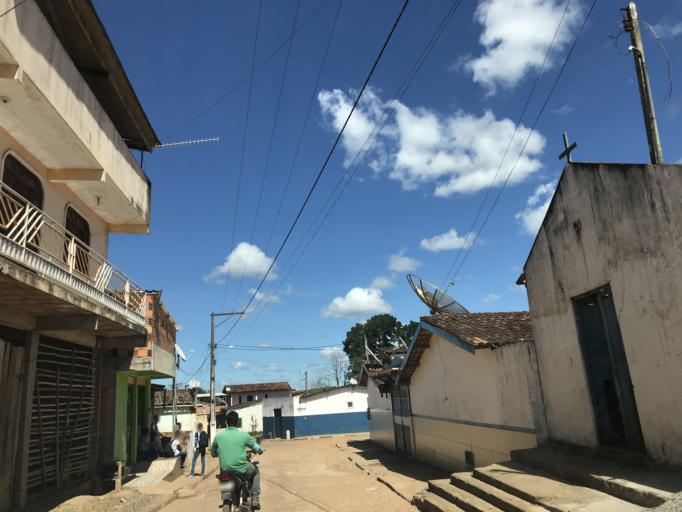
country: BR
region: Bahia
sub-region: Valenca
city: Valenca
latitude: -13.3234
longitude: -39.2414
